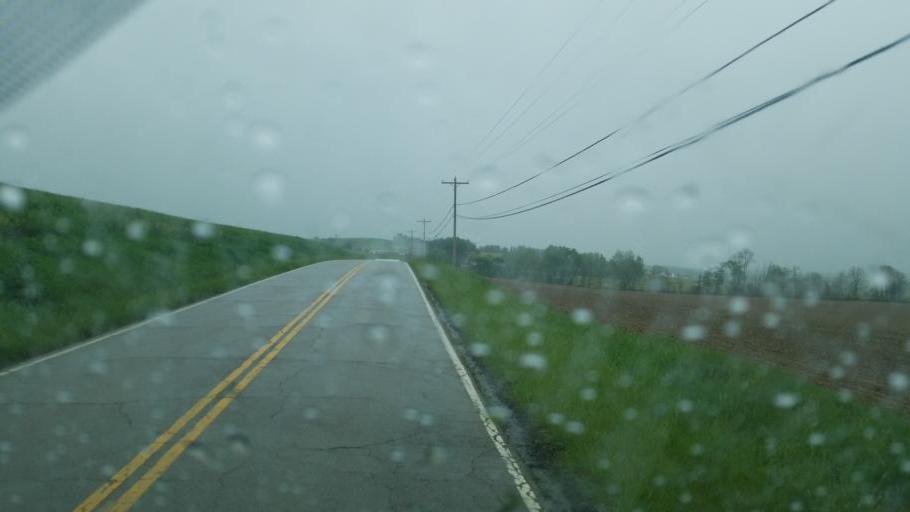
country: US
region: Ohio
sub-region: Muskingum County
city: Frazeysburg
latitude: 40.0855
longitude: -82.0831
